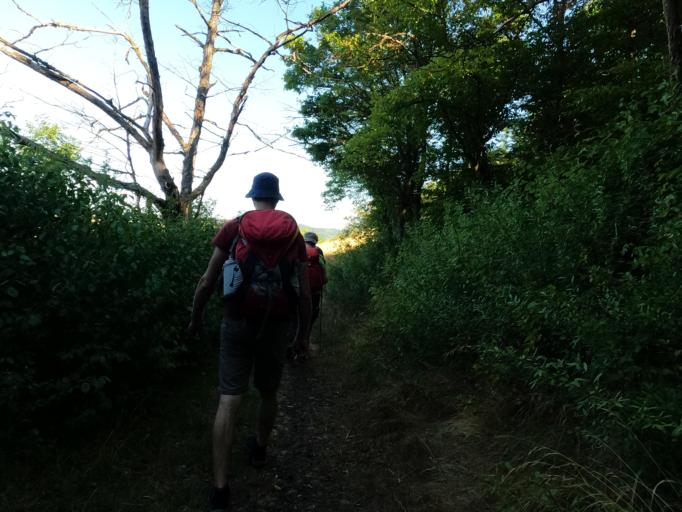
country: DE
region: Bavaria
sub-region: Regierungsbezirk Unterfranken
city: Zeitlofs
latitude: 50.3023
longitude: 9.6720
